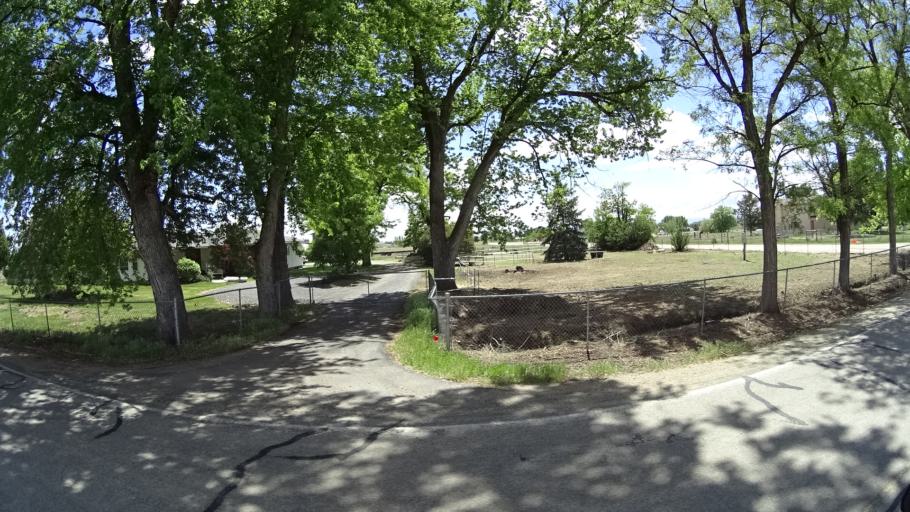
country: US
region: Idaho
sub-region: Ada County
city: Meridian
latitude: 43.5830
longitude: -116.4432
